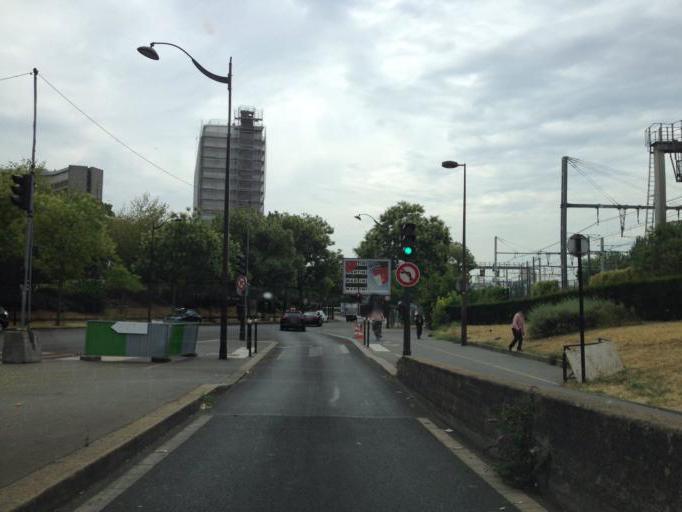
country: FR
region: Ile-de-France
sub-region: Departement des Hauts-de-Seine
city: Malakoff
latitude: 48.8269
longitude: 2.3037
